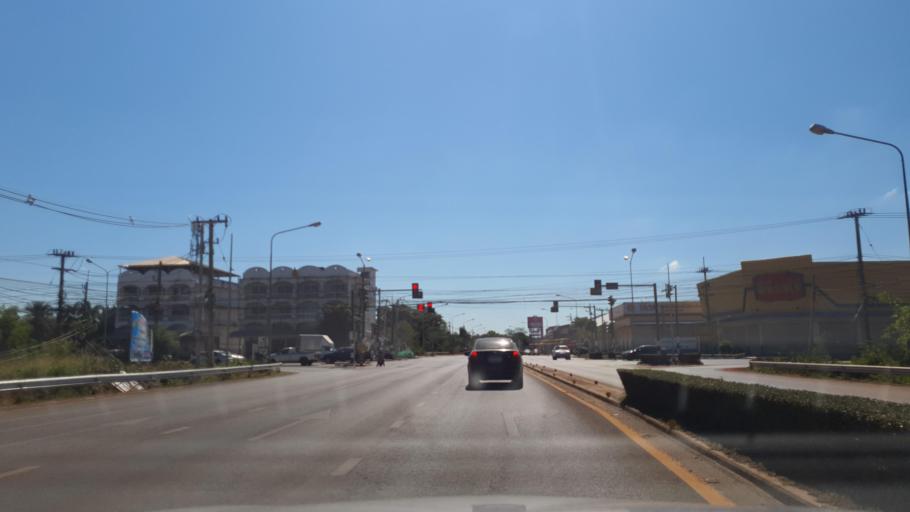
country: TH
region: Sakon Nakhon
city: Sakon Nakhon
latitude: 17.1485
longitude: 104.1298
